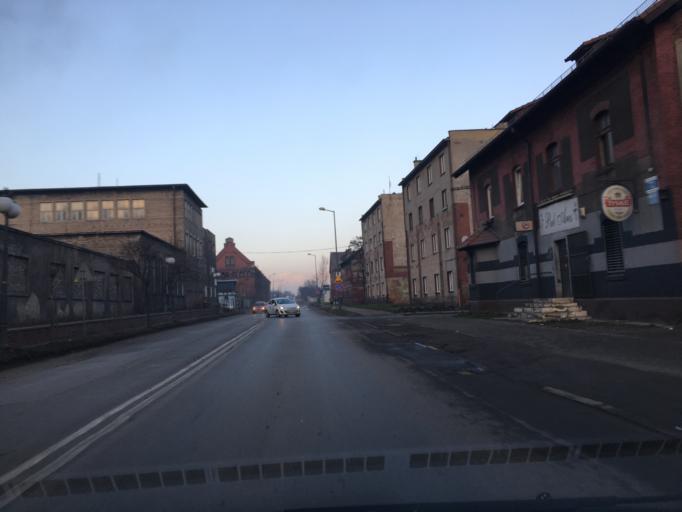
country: PL
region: Silesian Voivodeship
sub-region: Bytom
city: Bytom
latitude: 50.3405
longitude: 18.8707
